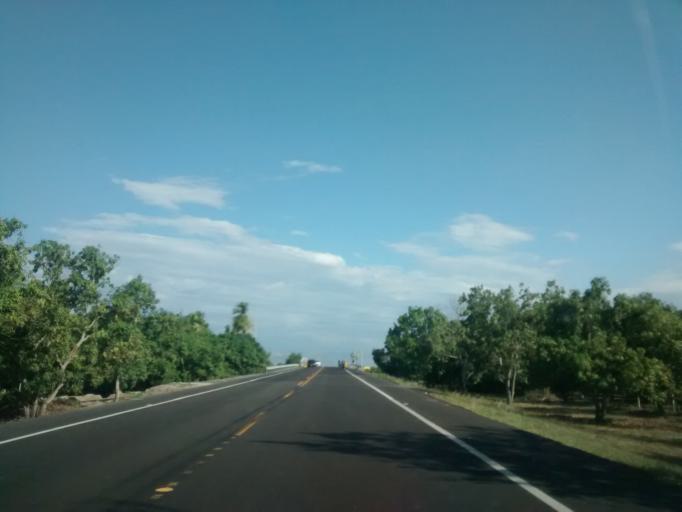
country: CO
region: Tolima
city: Espinal
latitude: 4.1547
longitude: -74.9156
